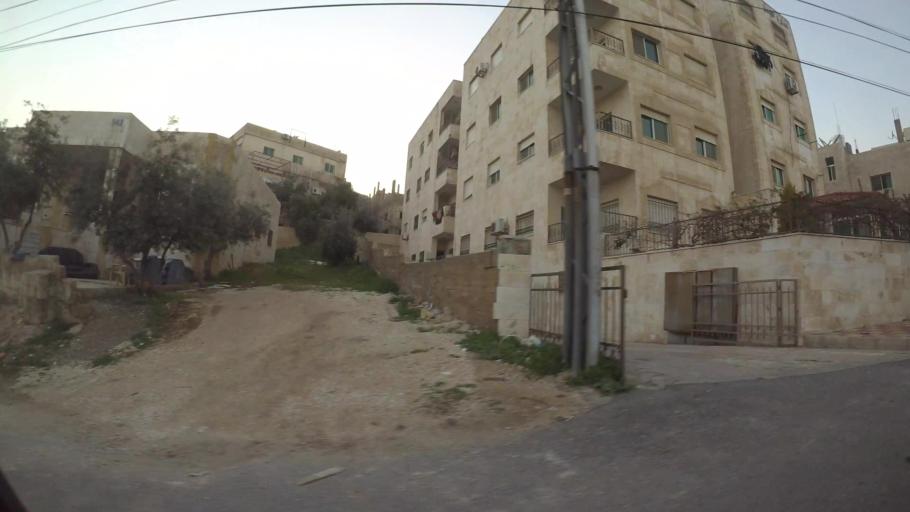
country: JO
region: Amman
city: Al Quwaysimah
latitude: 31.8951
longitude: 35.9290
